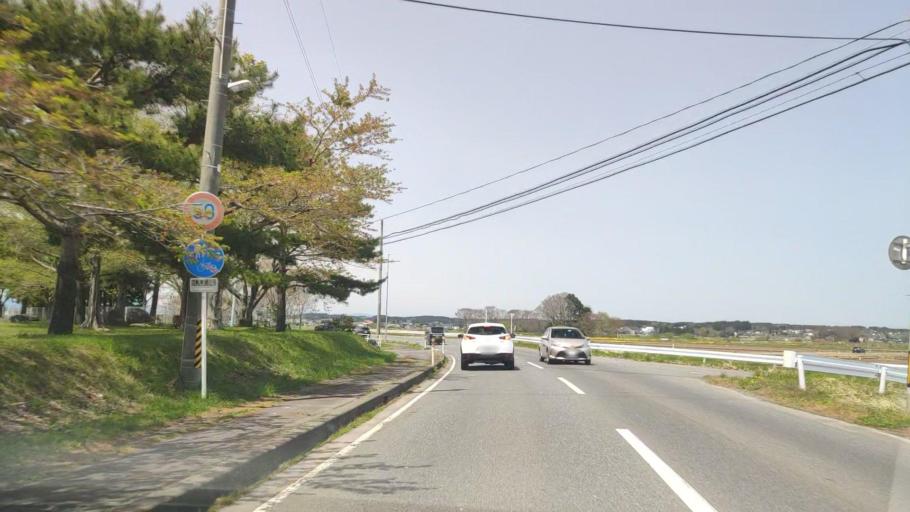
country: JP
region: Aomori
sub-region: Misawa Shi
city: Inuotose
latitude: 40.5935
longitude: 141.3418
